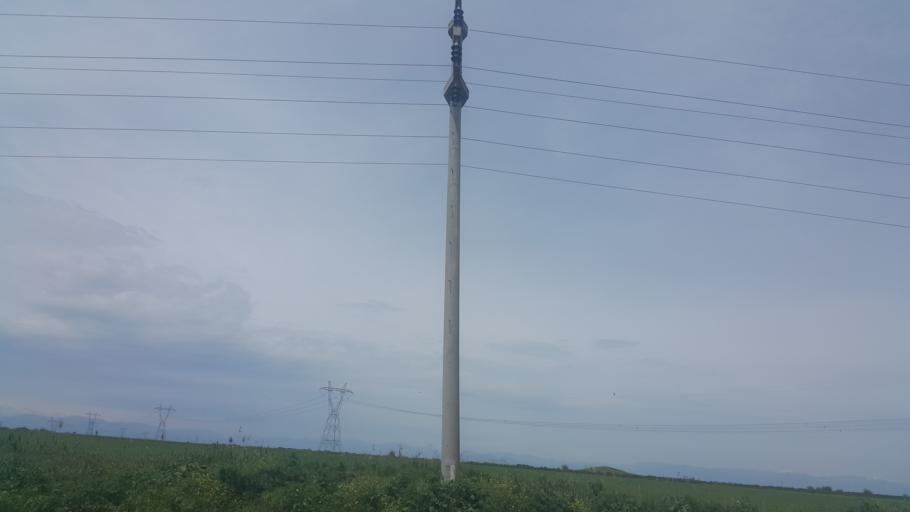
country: TR
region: Adana
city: Ceyhan
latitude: 37.0602
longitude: 35.9151
